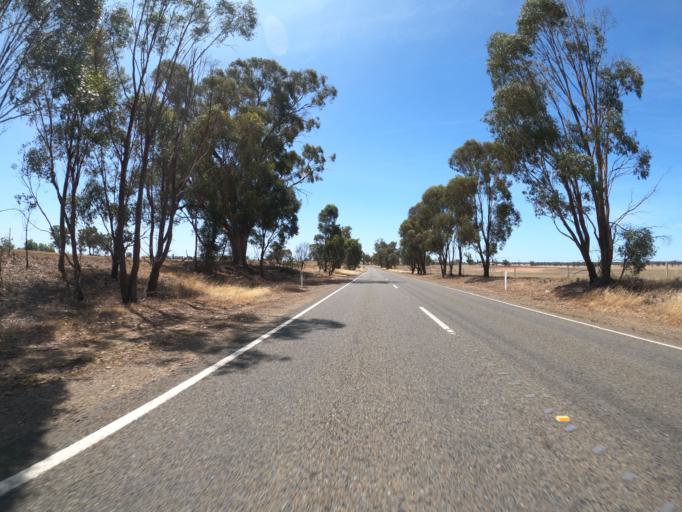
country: AU
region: Victoria
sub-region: Moira
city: Yarrawonga
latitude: -36.1014
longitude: 145.9929
